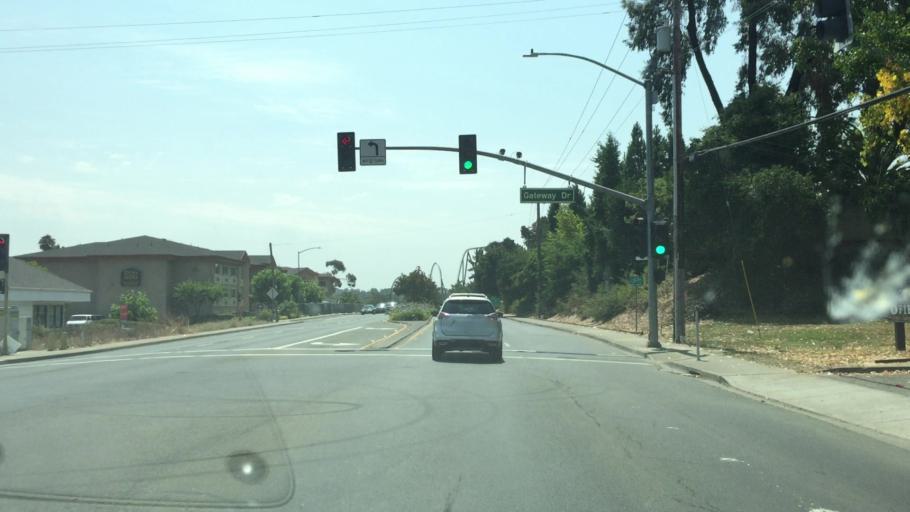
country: US
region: California
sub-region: Napa County
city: American Canyon
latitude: 38.1447
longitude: -122.2350
